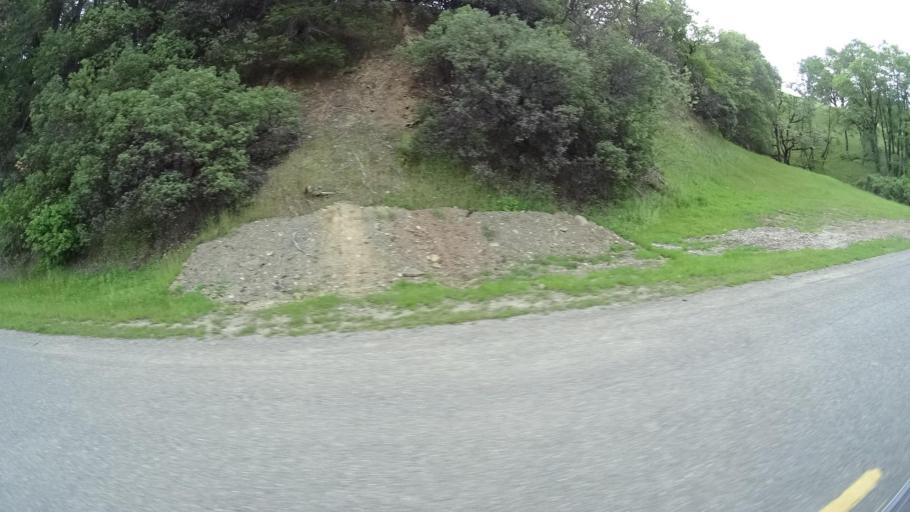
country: US
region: California
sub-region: Humboldt County
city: Redway
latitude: 40.2116
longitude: -123.5956
